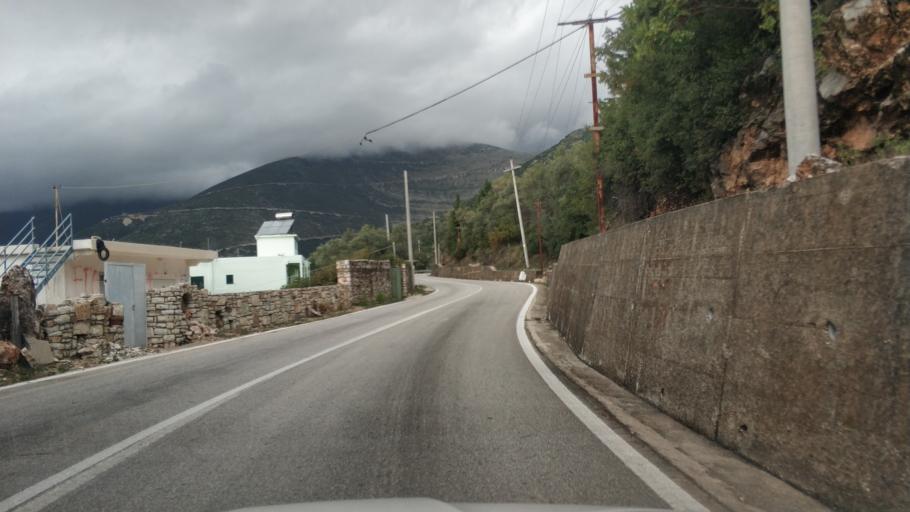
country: AL
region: Vlore
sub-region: Rrethi i Vlores
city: Vranisht
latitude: 40.1639
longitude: 19.6211
